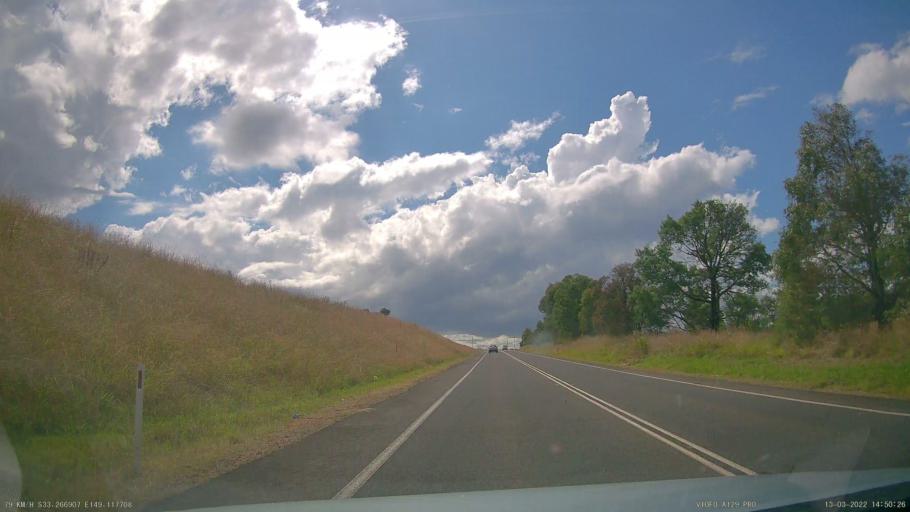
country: AU
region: New South Wales
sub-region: Orange Municipality
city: Orange
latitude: -33.2667
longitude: 149.1176
